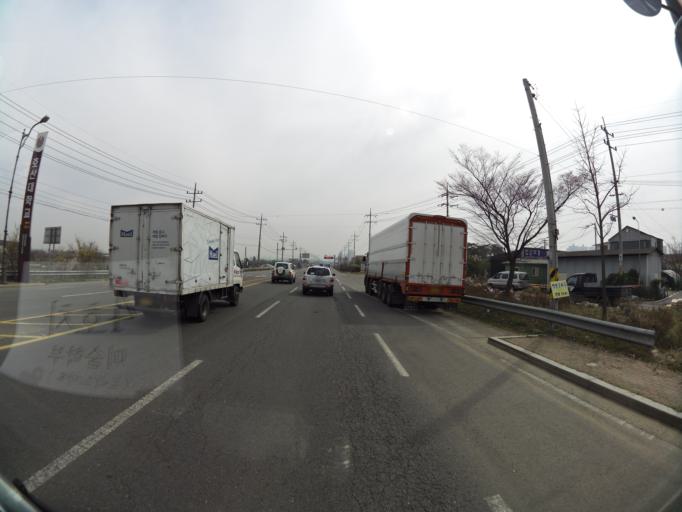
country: KR
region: Gyeongsangbuk-do
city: Hayang
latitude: 35.8726
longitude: 128.7819
